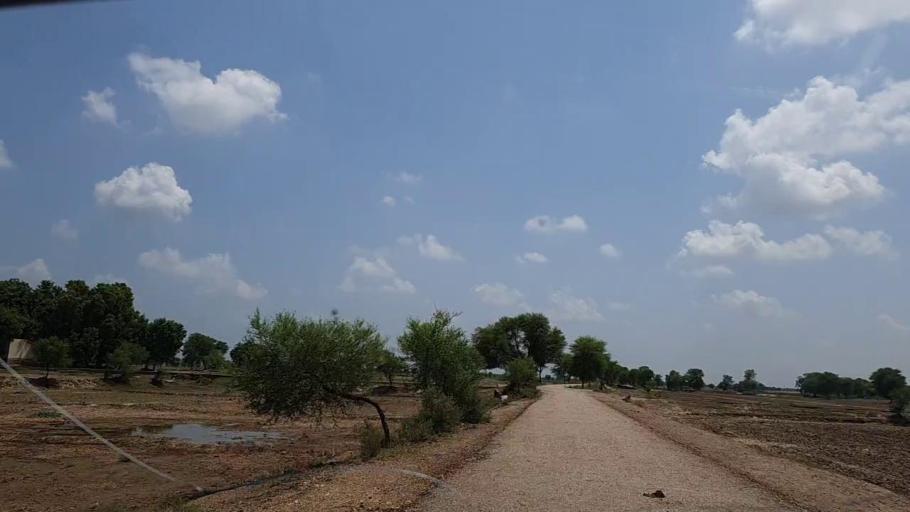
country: PK
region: Sindh
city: Tharu Shah
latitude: 27.0204
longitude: 68.0729
